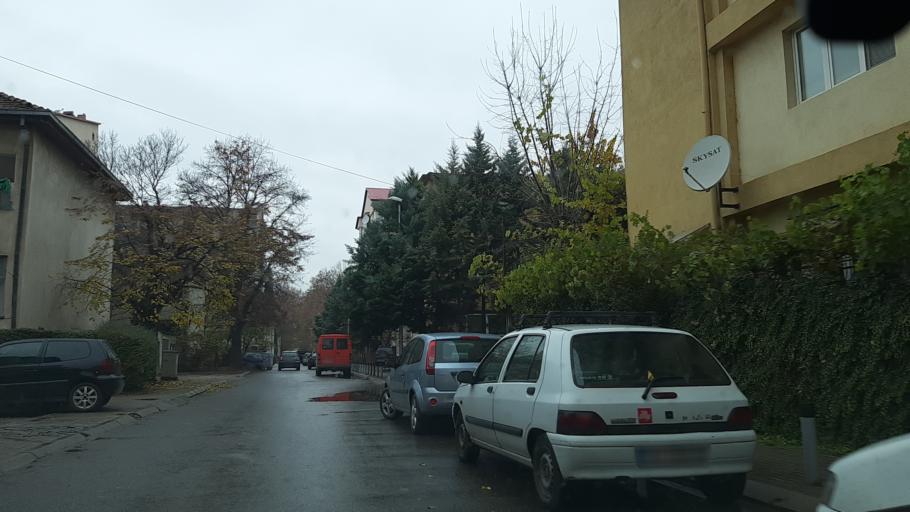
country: MK
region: Karpos
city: Skopje
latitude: 41.9861
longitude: 21.4479
